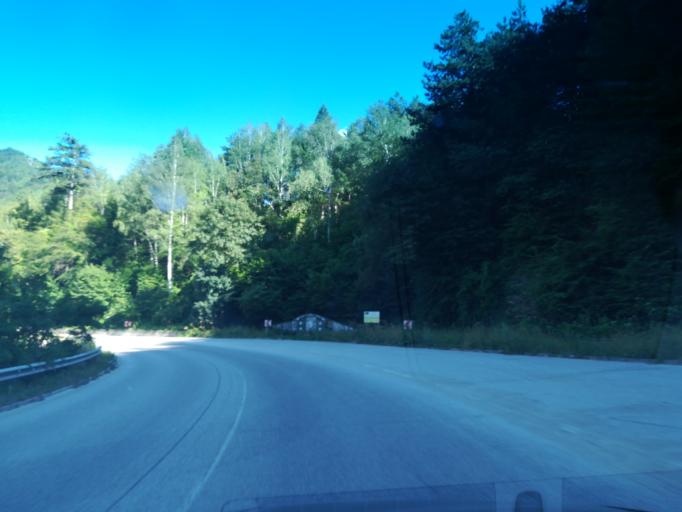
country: BG
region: Smolyan
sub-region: Obshtina Chepelare
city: Chepelare
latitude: 41.8361
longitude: 24.6800
